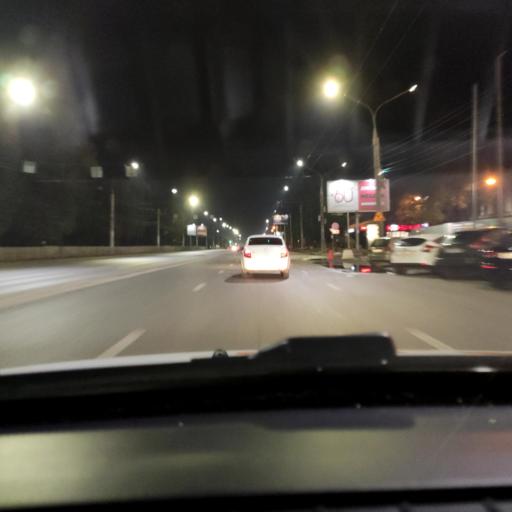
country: RU
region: Voronezj
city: Voronezh
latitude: 51.6978
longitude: 39.2722
